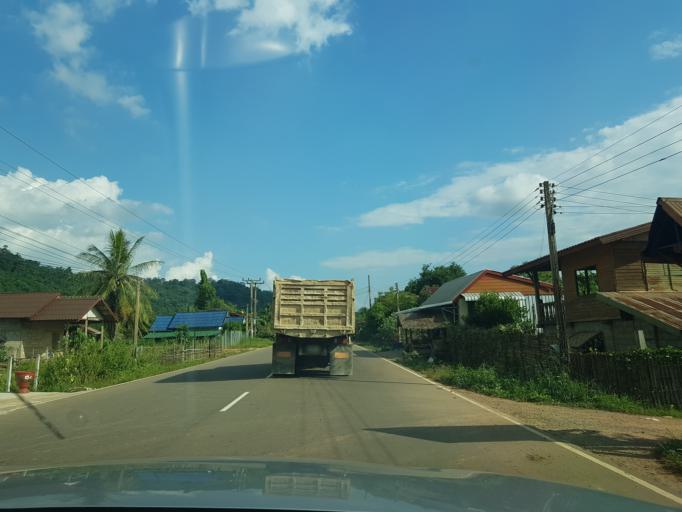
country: TH
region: Nong Khai
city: Sangkhom
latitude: 18.0178
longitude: 102.3944
